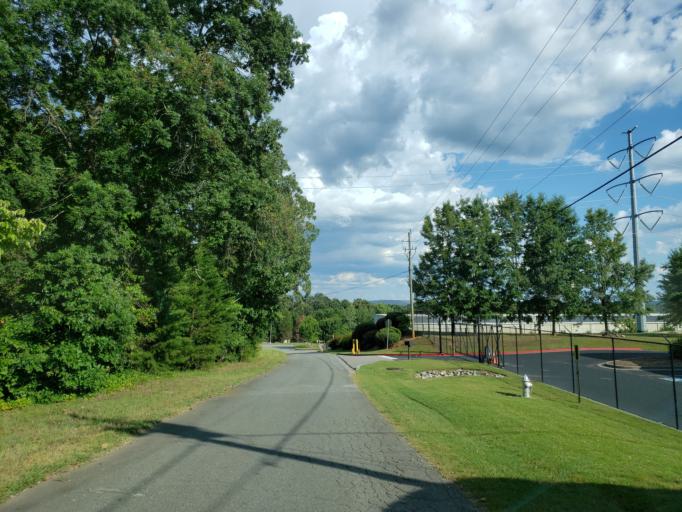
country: US
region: Georgia
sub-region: Cherokee County
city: Ball Ground
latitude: 34.3079
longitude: -84.4202
